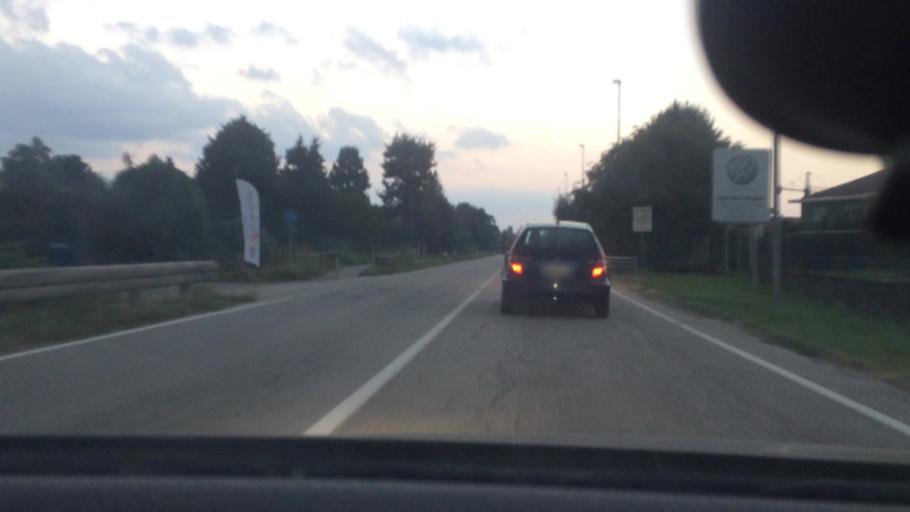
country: IT
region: Lombardy
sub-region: Citta metropolitana di Milano
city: Buscate
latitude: 45.5449
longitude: 8.8019
